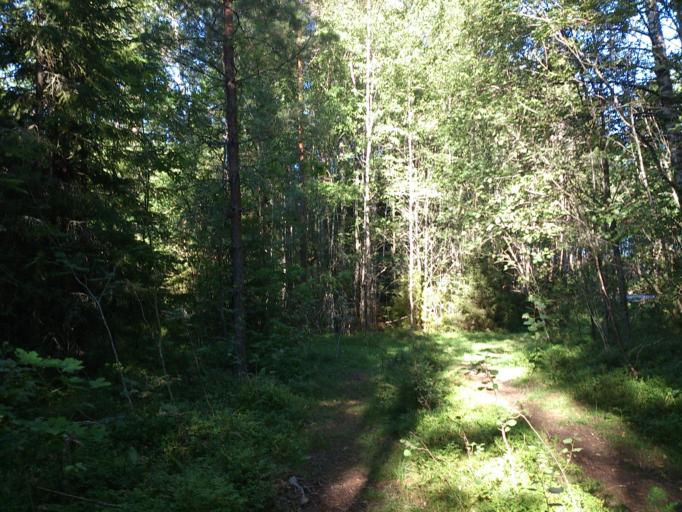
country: SE
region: Uppsala
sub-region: Uppsala Kommun
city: Saevja
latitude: 59.7762
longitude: 17.6607
